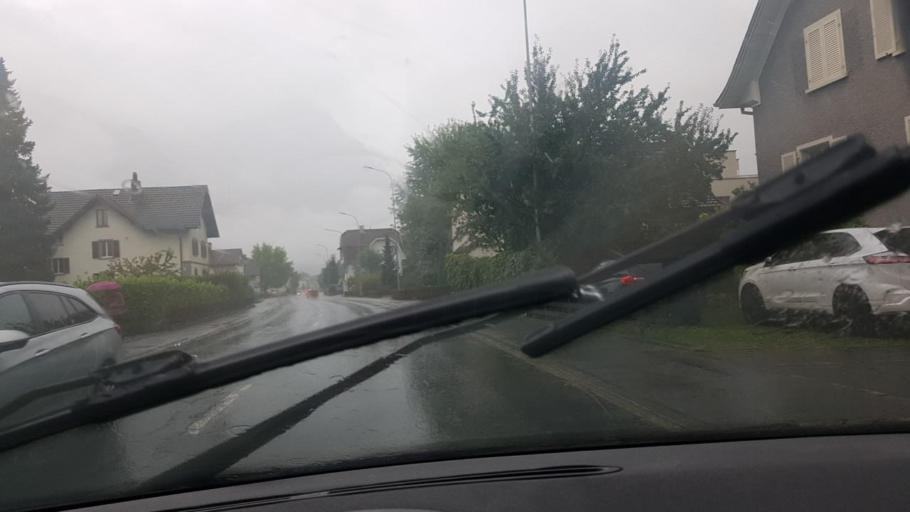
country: LI
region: Triesen
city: Triesen
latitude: 47.1143
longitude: 9.5236
